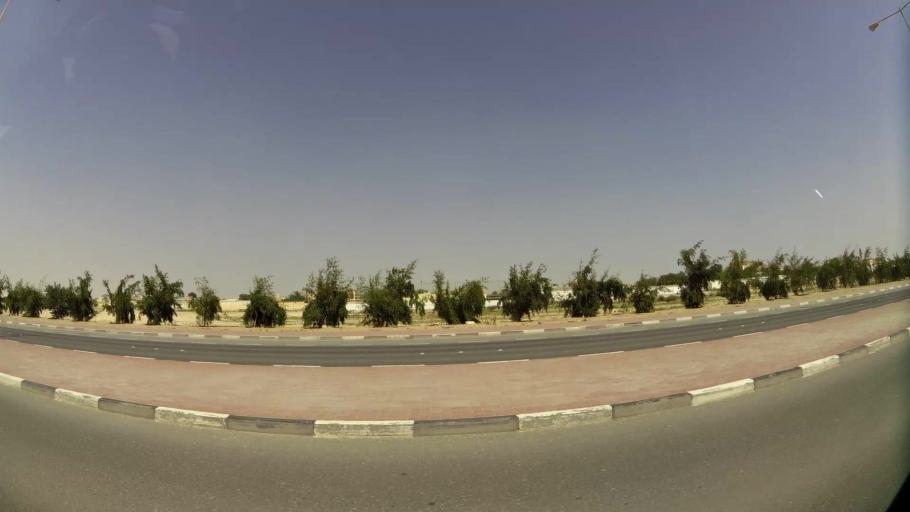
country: QA
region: Baladiyat Umm Salal
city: Umm Salal Muhammad
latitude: 25.3867
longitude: 51.4239
